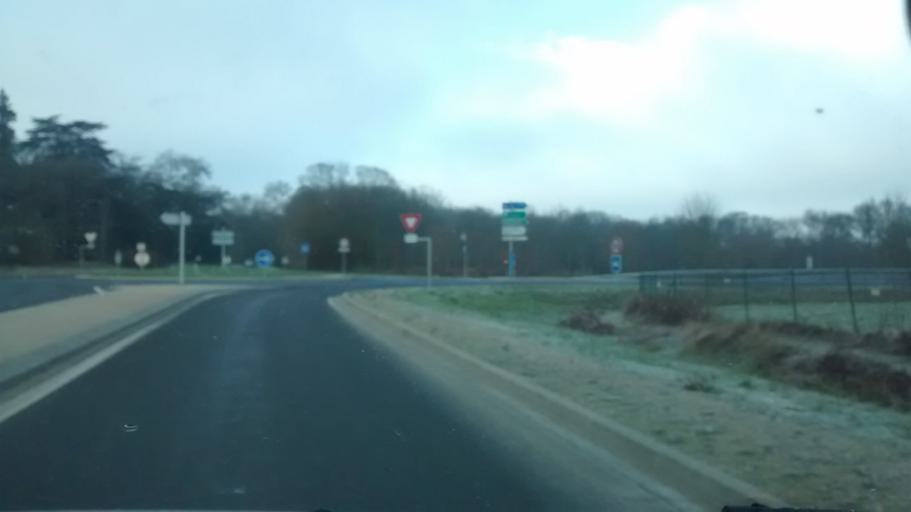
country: FR
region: Centre
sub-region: Departement d'Indre-et-Loire
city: Joue-les-Tours
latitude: 47.3674
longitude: 0.6536
